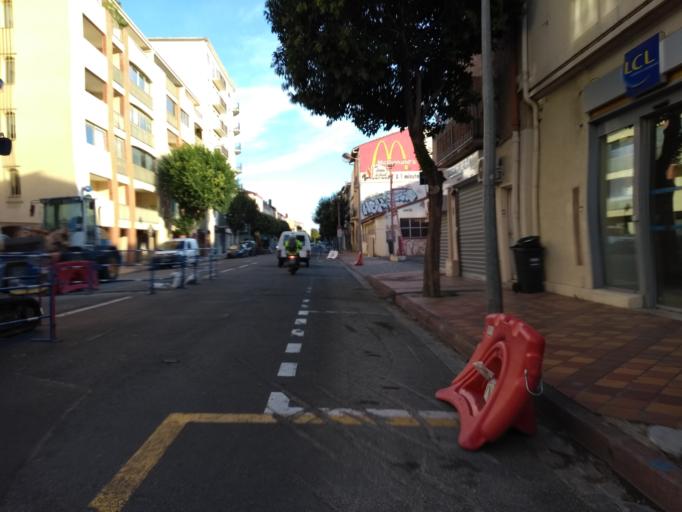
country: FR
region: Languedoc-Roussillon
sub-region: Departement des Pyrenees-Orientales
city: Perpignan
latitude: 42.7084
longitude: 2.8910
